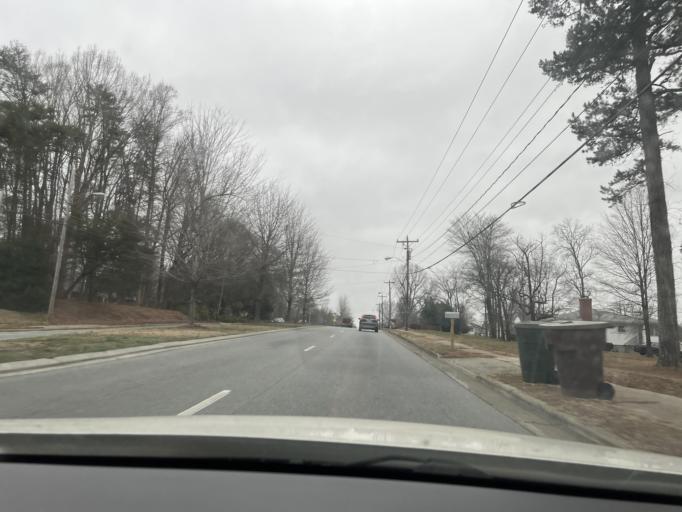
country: US
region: North Carolina
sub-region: Guilford County
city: Greensboro
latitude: 36.0175
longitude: -79.7928
